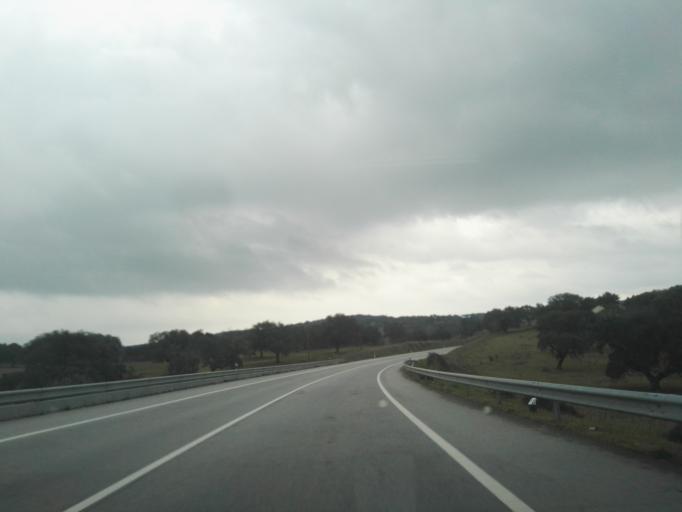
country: PT
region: Portalegre
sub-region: Portalegre
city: Alegrete
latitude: 39.1865
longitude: -7.3479
